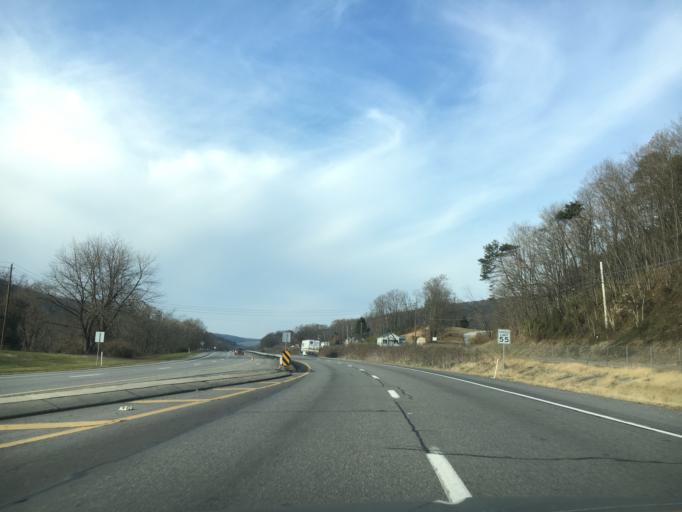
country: US
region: Pennsylvania
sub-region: Montour County
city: Danville
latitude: 40.9722
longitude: -76.6169
